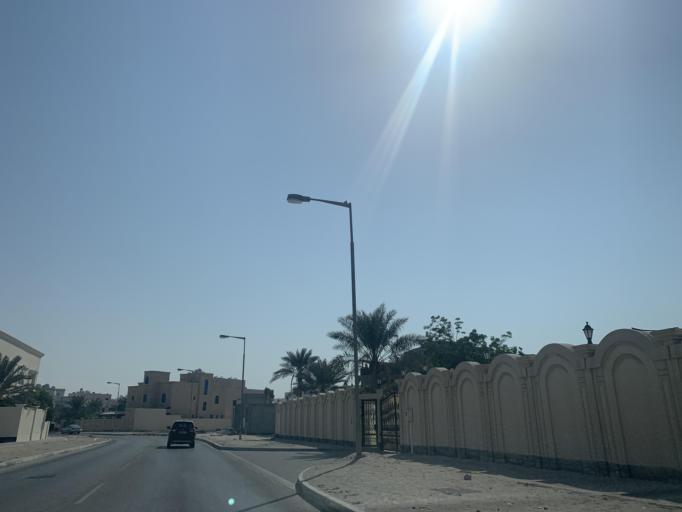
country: BH
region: Central Governorate
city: Madinat Hamad
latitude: 26.1341
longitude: 50.4917
